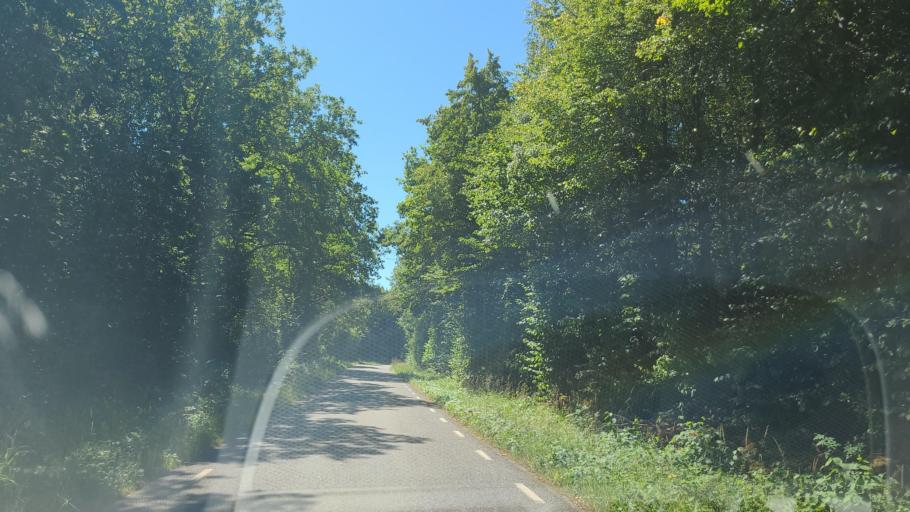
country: SE
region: Kalmar
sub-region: Borgholms Kommun
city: Borgholm
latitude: 56.7518
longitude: 16.6586
